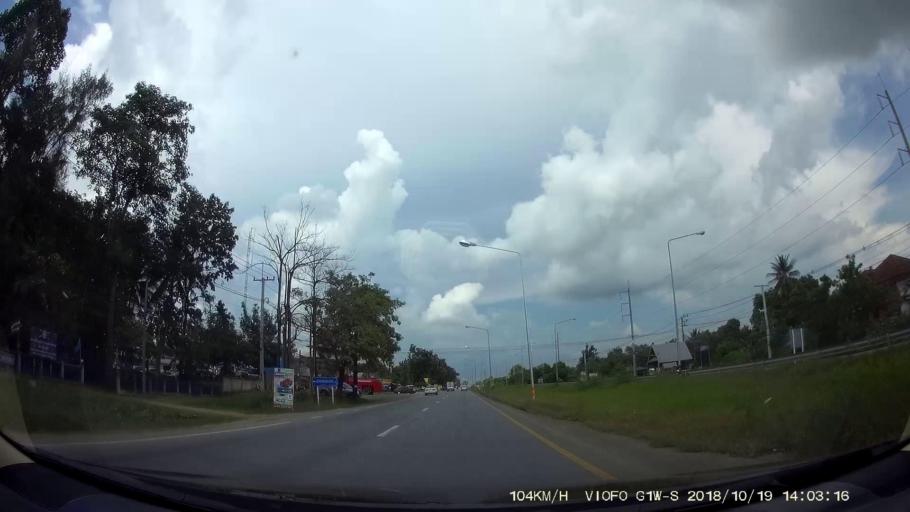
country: TH
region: Chaiyaphum
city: Chaiyaphum
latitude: 15.8505
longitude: 102.0686
